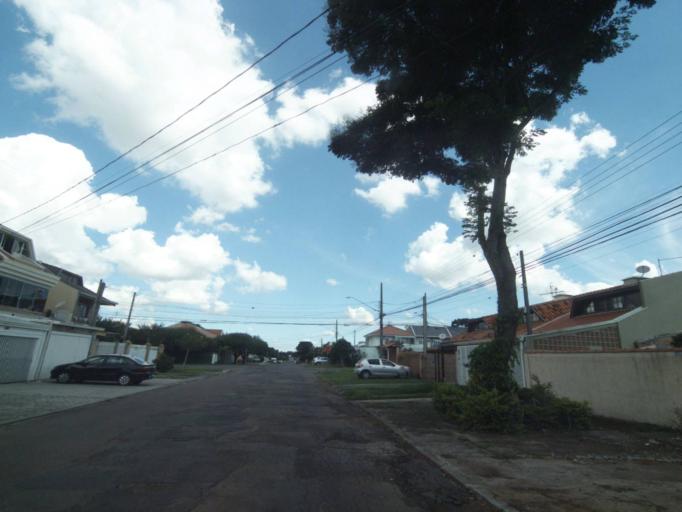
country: BR
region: Parana
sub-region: Pinhais
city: Pinhais
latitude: -25.4591
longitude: -49.2086
